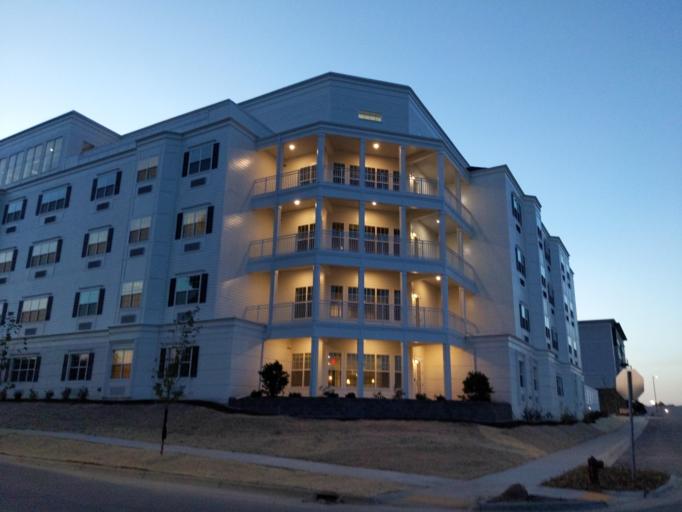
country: US
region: Michigan
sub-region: Ingham County
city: East Lansing
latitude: 42.7316
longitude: -84.5068
